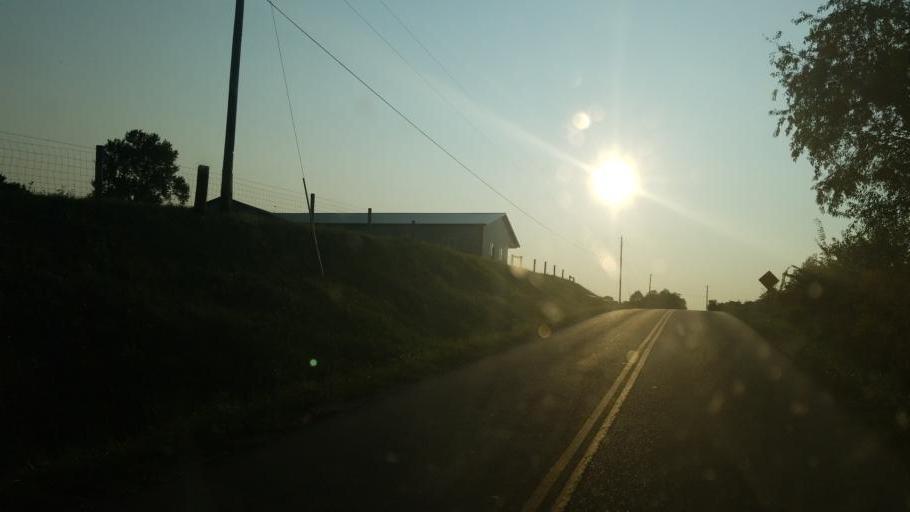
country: US
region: Ohio
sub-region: Wayne County
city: Shreve
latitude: 40.6678
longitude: -81.9771
